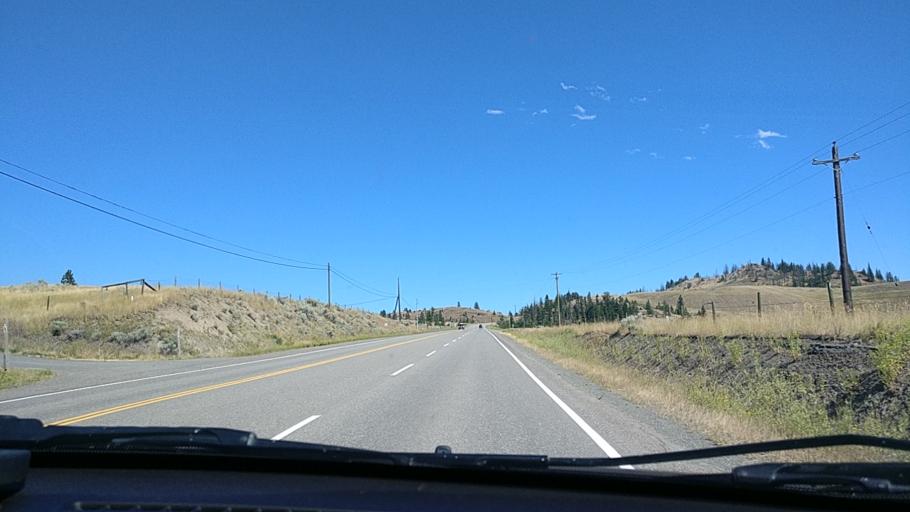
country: CA
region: British Columbia
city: Kamloops
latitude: 50.6625
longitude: -120.5497
